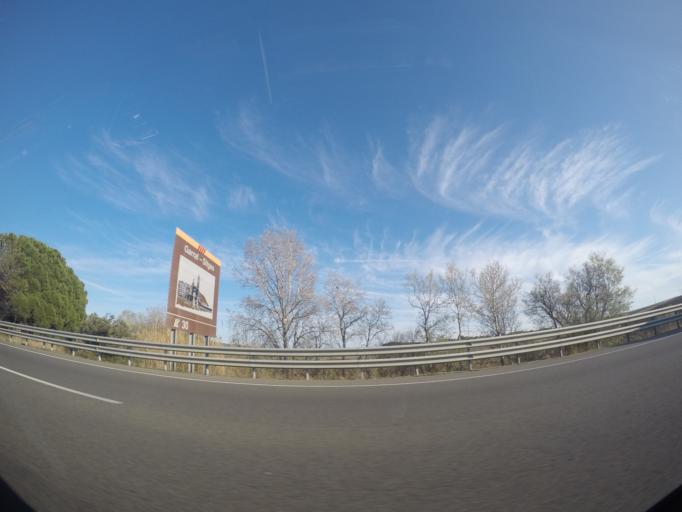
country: ES
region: Catalonia
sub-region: Provincia de Barcelona
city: Castellet
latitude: 41.3053
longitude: 1.6168
